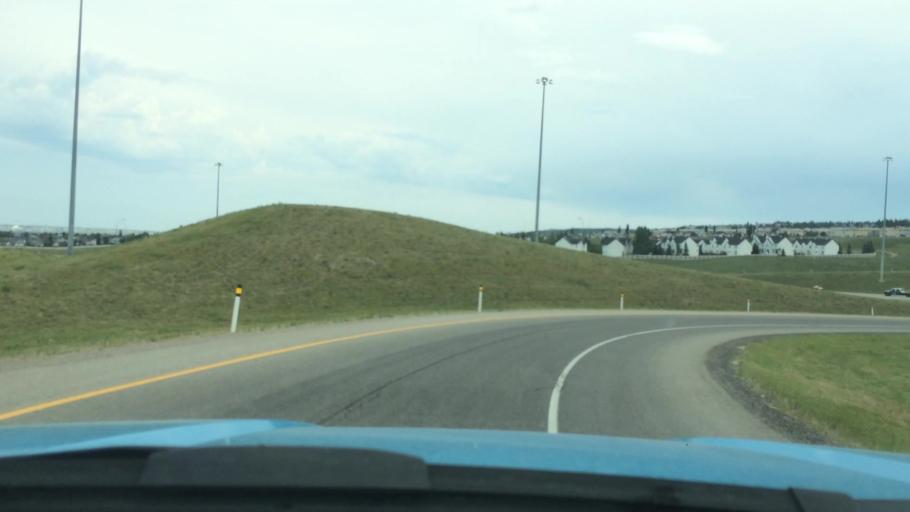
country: CA
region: Alberta
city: Calgary
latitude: 51.1540
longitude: -114.1387
